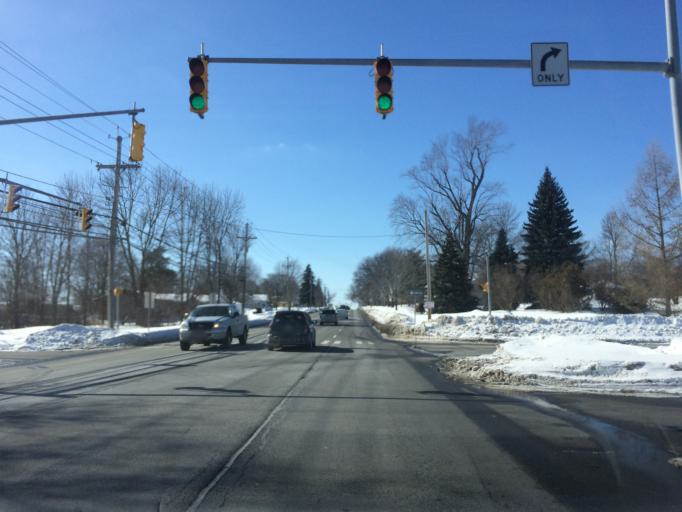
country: US
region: New York
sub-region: Monroe County
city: Rochester
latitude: 43.0951
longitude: -77.6058
